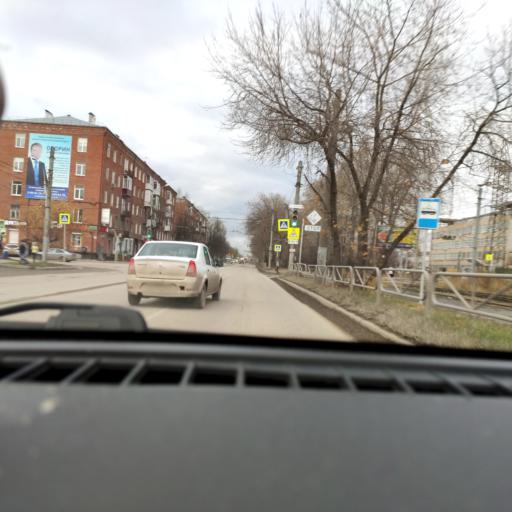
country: RU
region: Perm
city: Perm
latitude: 57.9654
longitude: 56.2446
